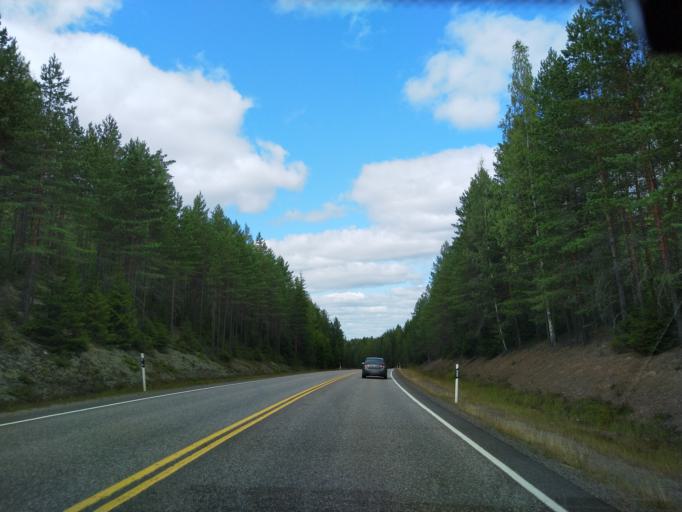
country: FI
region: Haeme
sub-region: Riihimaeki
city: Loppi
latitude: 60.7402
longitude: 24.3637
